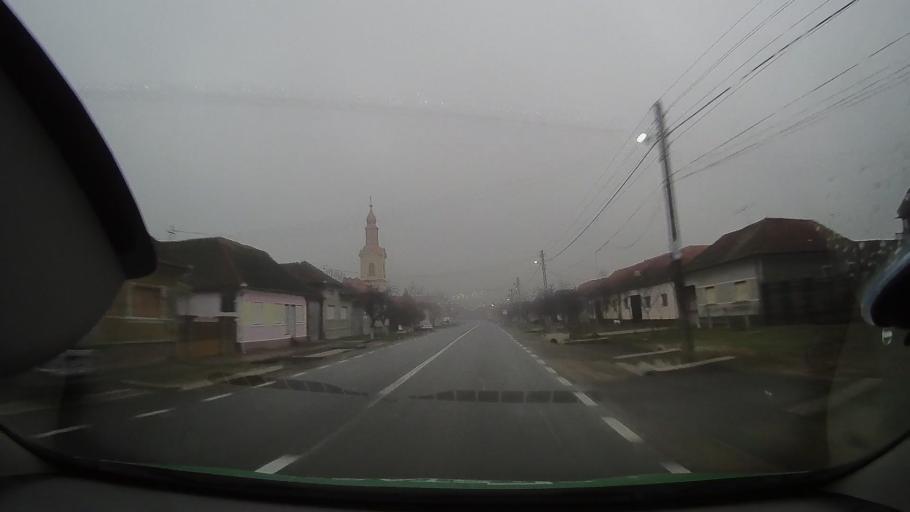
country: RO
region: Bihor
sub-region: Comuna Olcea
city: Calacea
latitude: 46.6381
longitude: 21.9559
